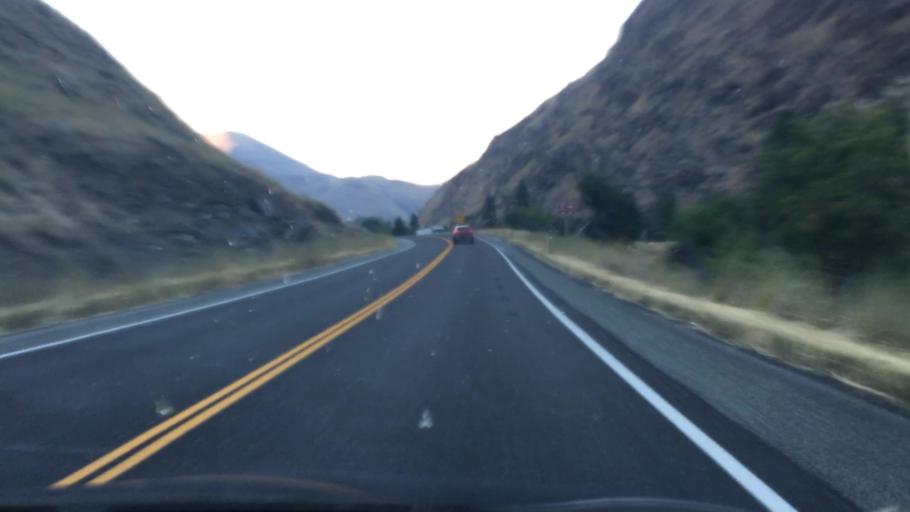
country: US
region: Idaho
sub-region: Valley County
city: McCall
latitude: 45.3618
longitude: -116.3604
